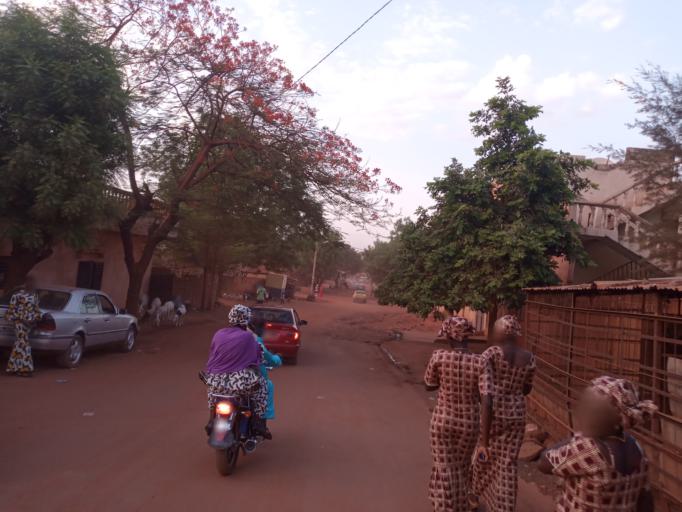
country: ML
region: Bamako
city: Bamako
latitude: 12.5807
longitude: -8.0229
